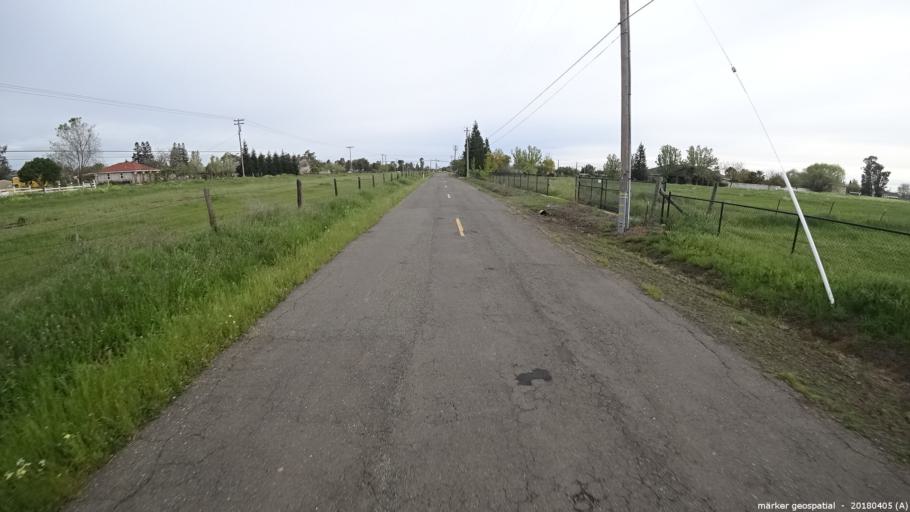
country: US
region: California
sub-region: Sacramento County
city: Herald
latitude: 38.2895
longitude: -121.2444
